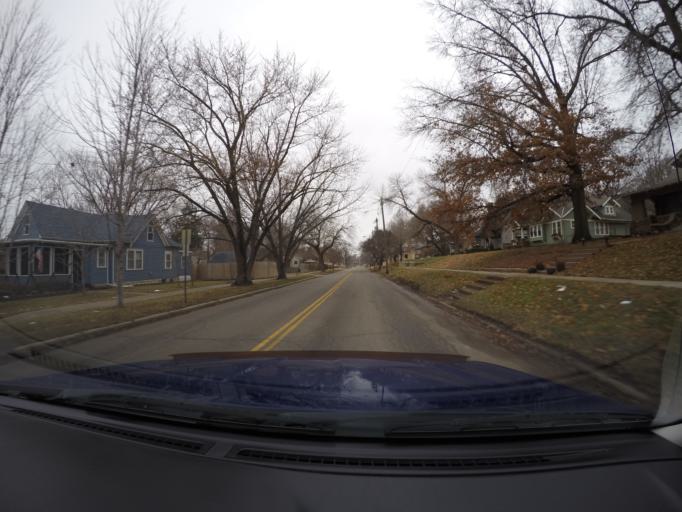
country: US
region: Kansas
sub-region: Riley County
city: Manhattan
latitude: 39.1785
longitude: -96.5833
